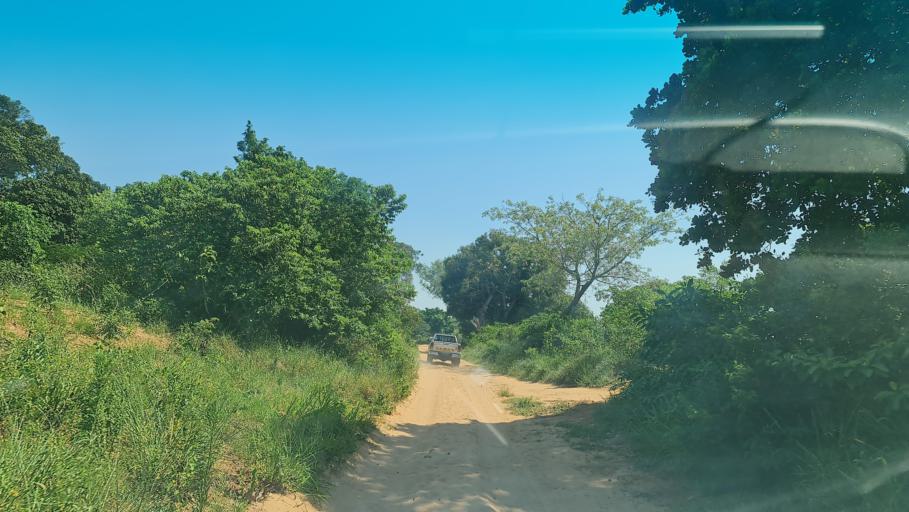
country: MZ
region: Gaza
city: Macia
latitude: -25.0883
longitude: 33.0982
